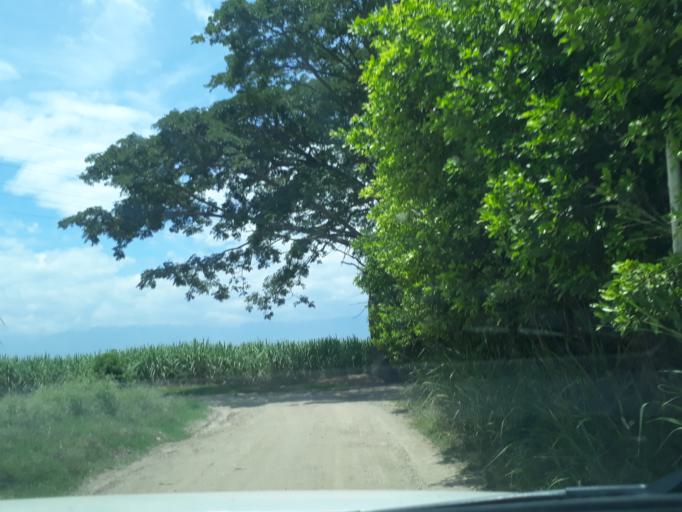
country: CO
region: Valle del Cauca
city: Cali
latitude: 3.3671
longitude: -76.4748
